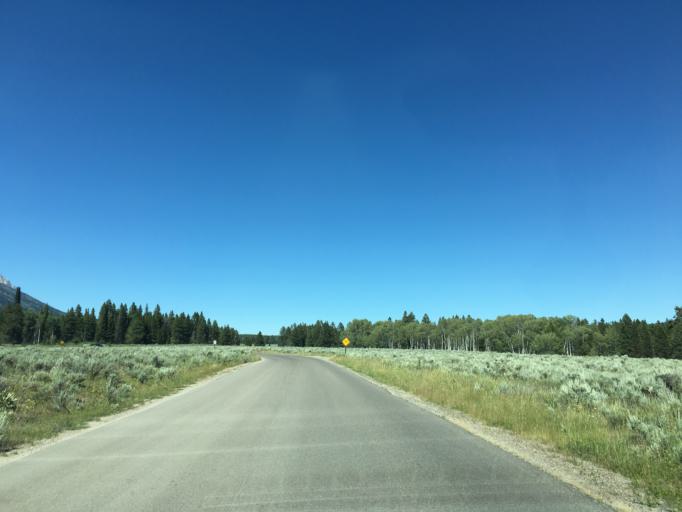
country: US
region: Wyoming
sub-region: Teton County
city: Moose Wilson Road
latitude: 43.6026
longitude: -110.7936
